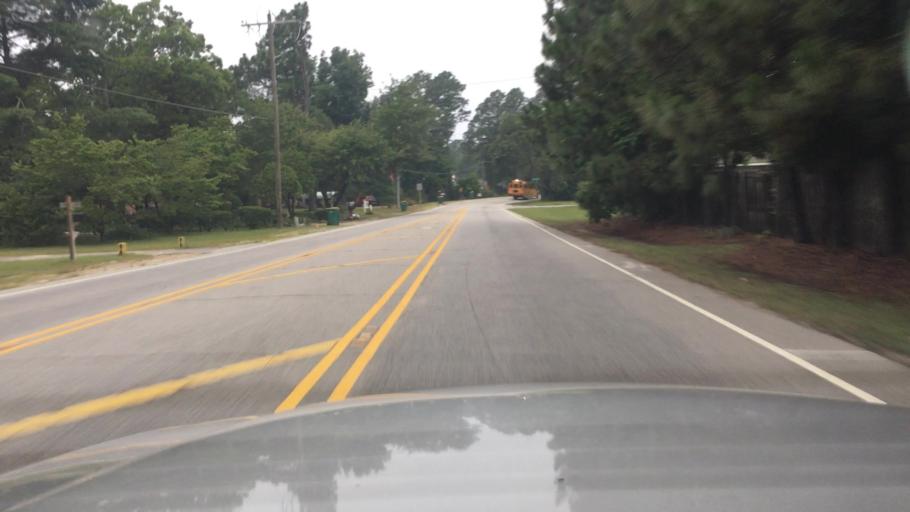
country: US
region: North Carolina
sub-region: Cumberland County
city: Hope Mills
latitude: 34.9728
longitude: -78.9624
